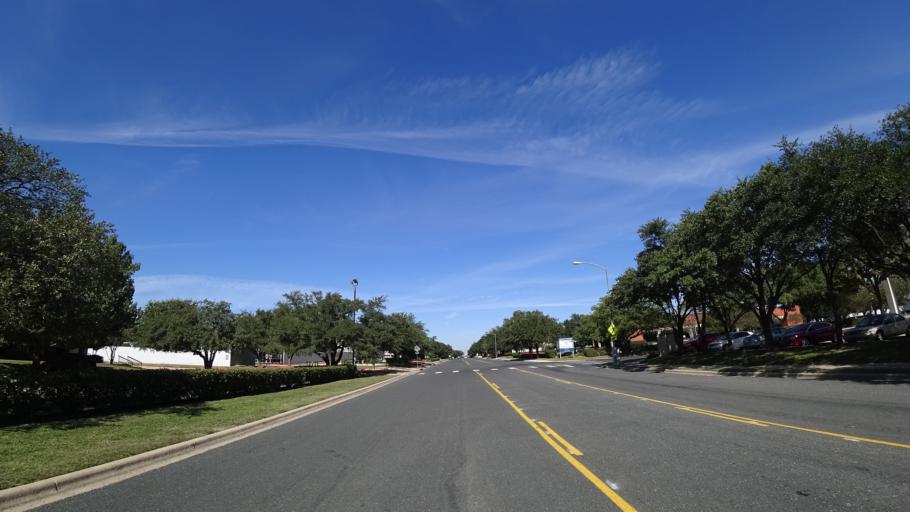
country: US
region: Texas
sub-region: Travis County
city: Austin
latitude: 30.2098
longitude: -97.7438
